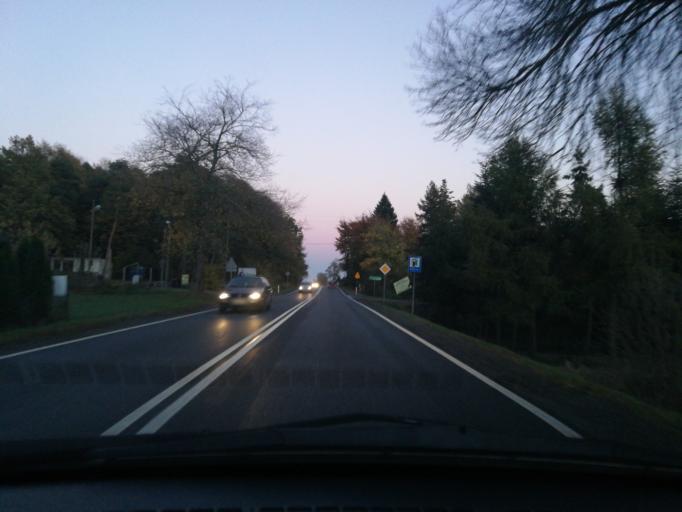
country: PL
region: Lodz Voivodeship
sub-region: Powiat brzezinski
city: Brzeziny
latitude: 51.8042
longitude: 19.6946
